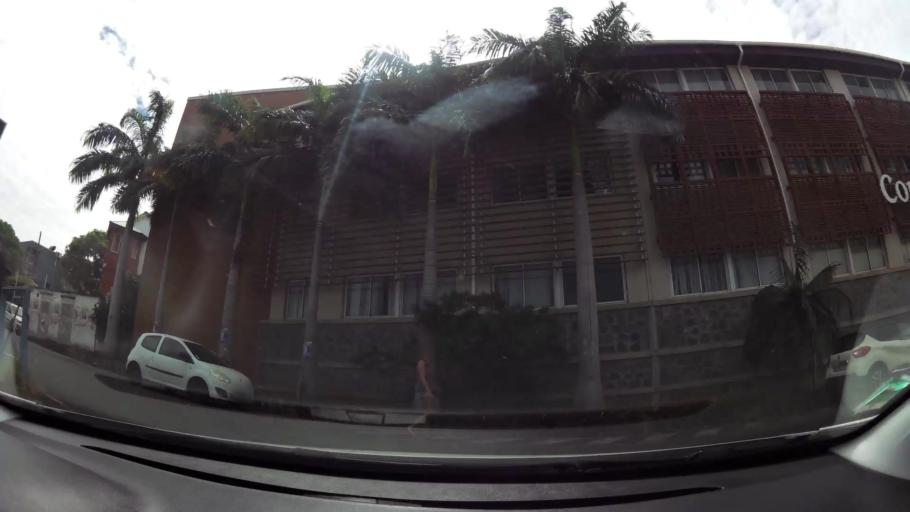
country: YT
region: Mamoudzou
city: Mamoudzou
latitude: -12.7797
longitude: 45.2313
